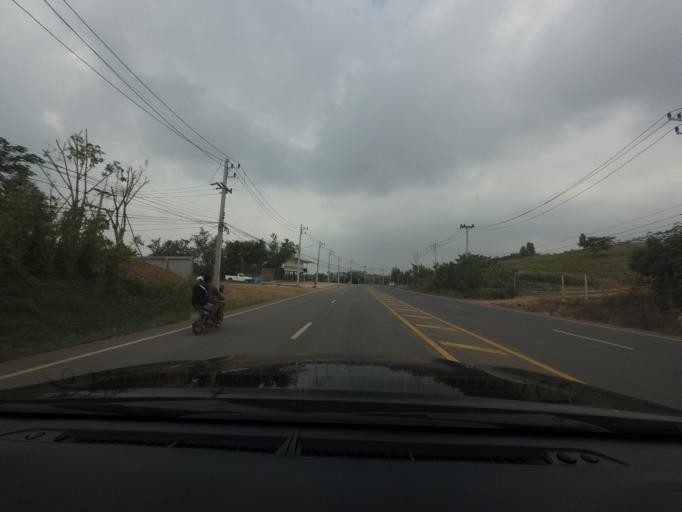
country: TH
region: Nakhon Ratchasima
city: Pak Chong
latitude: 14.5146
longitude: 101.5321
